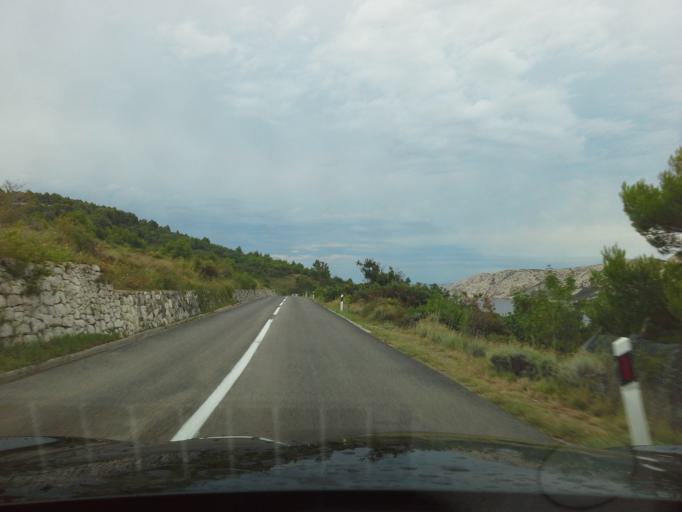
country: HR
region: Primorsko-Goranska
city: Banjol
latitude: 44.7167
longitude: 14.8251
